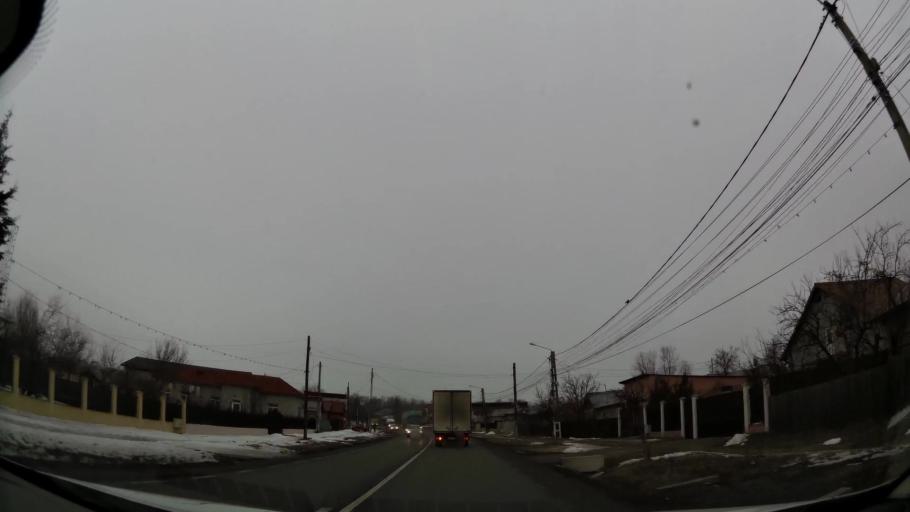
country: RO
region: Dambovita
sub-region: Comuna Racari
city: Racari
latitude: 44.6342
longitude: 25.7256
